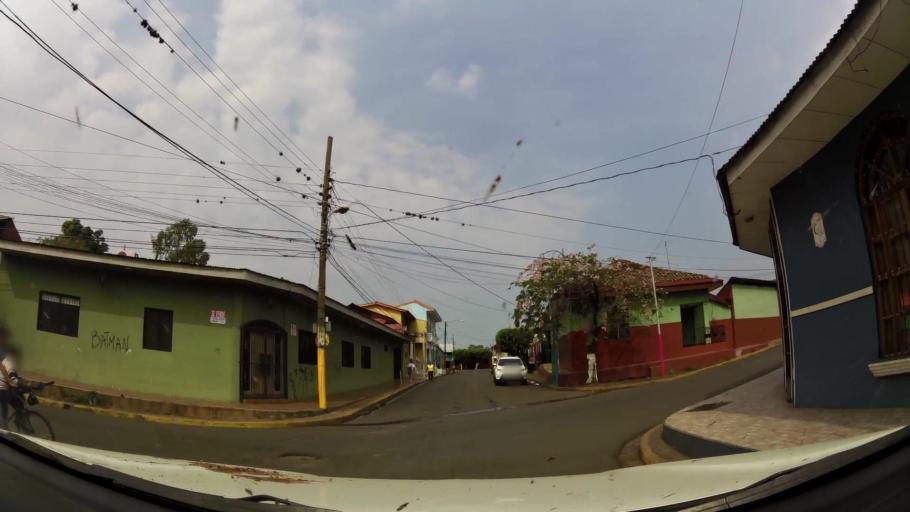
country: NI
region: Masaya
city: Masaya
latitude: 11.9751
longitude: -86.0976
